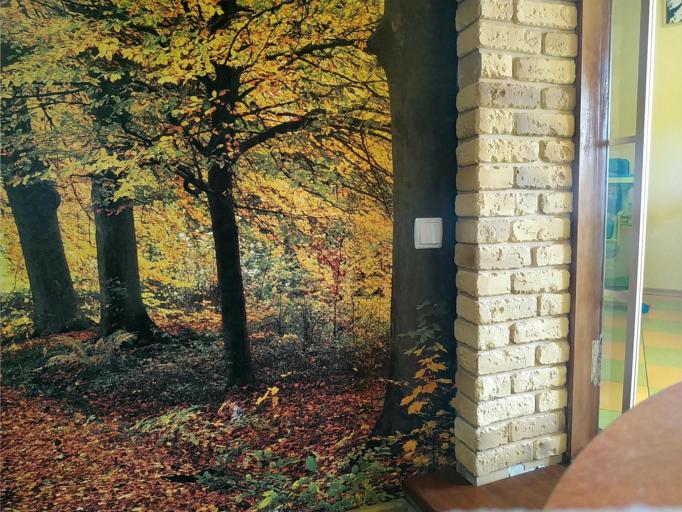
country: RU
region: Smolensk
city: Katyn'
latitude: 54.9458
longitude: 31.7161
